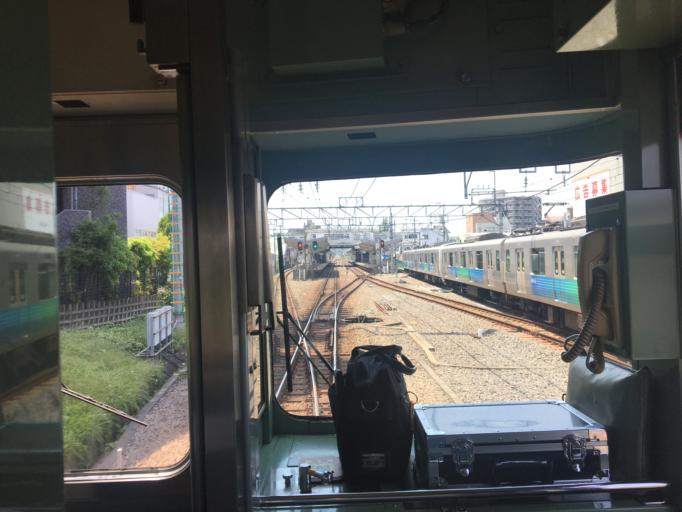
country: JP
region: Tokyo
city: Tanashicho
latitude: 35.7716
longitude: 139.5217
